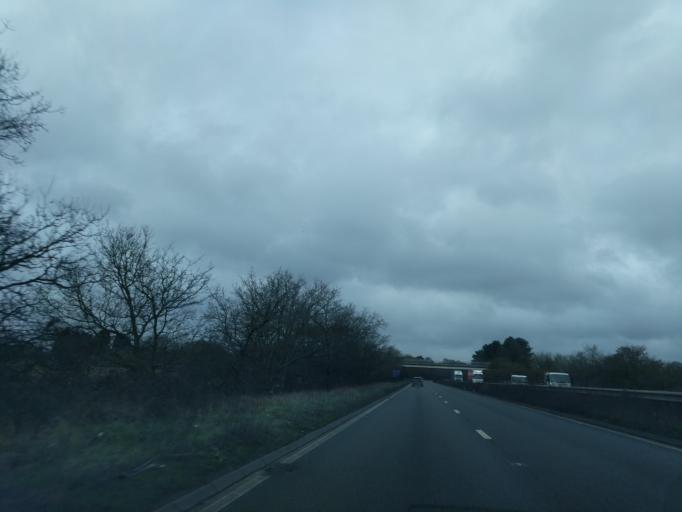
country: GB
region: England
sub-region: Staffordshire
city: Lichfield
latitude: 52.6572
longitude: -1.8189
